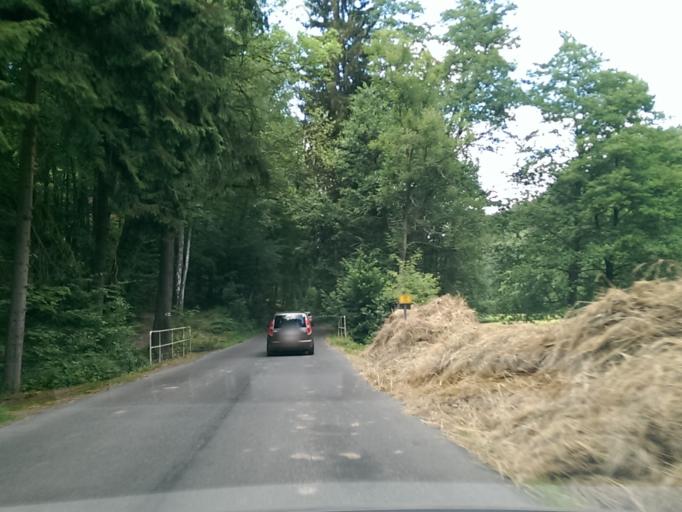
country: CZ
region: Central Bohemia
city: Mseno
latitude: 50.4162
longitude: 14.5794
